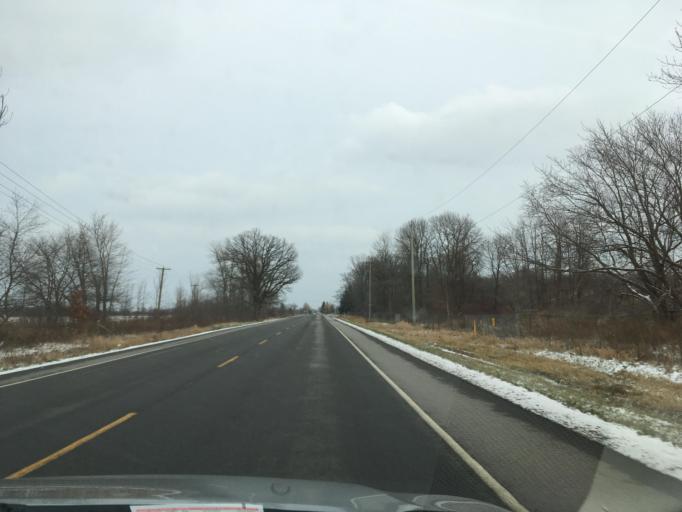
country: CA
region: Ontario
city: Norfolk County
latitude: 42.8153
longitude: -80.0450
